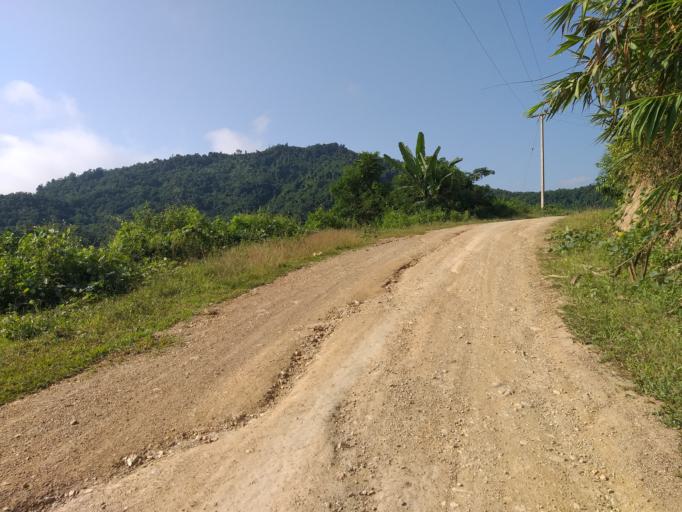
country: LA
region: Phongsali
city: Khoa
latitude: 21.2007
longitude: 102.6829
